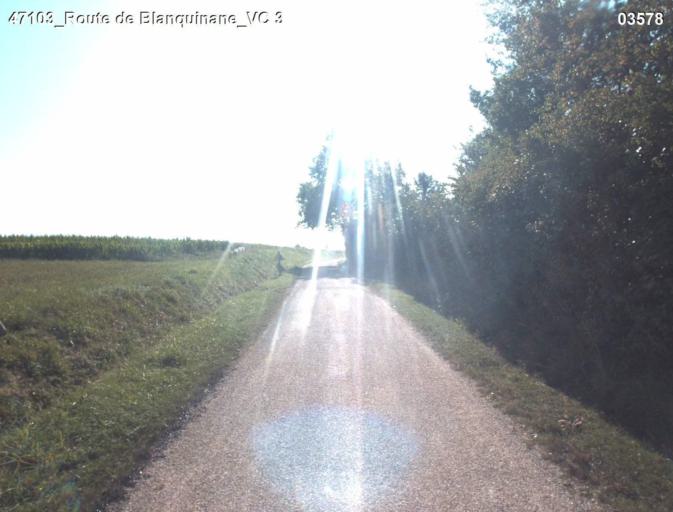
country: FR
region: Aquitaine
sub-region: Departement du Lot-et-Garonne
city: Nerac
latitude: 44.0909
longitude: 0.3236
